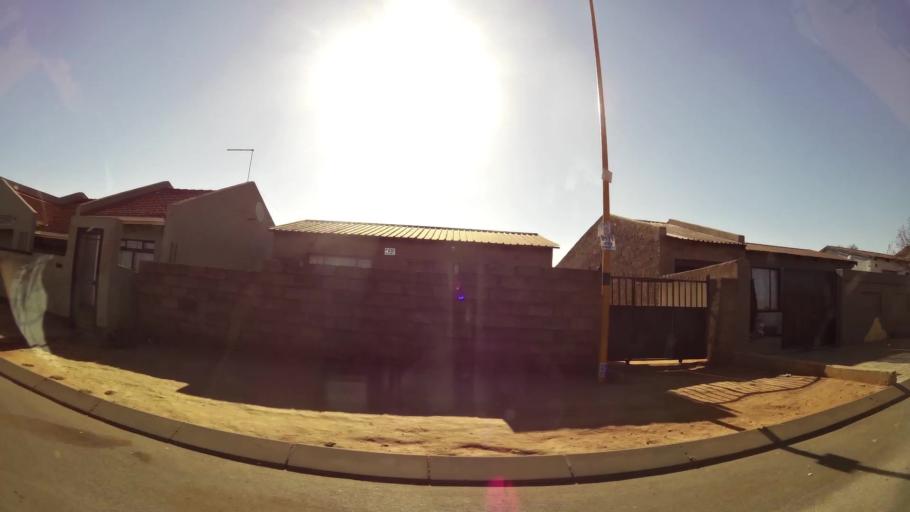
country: ZA
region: Gauteng
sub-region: Ekurhuleni Metropolitan Municipality
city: Tembisa
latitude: -26.0289
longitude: 28.2233
